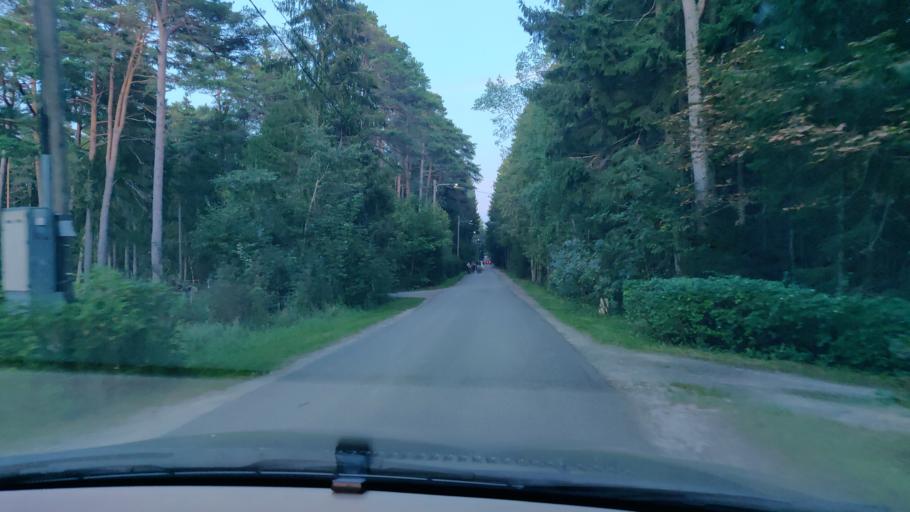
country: EE
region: Harju
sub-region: Keila linn
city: Keila
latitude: 59.3470
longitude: 24.2557
